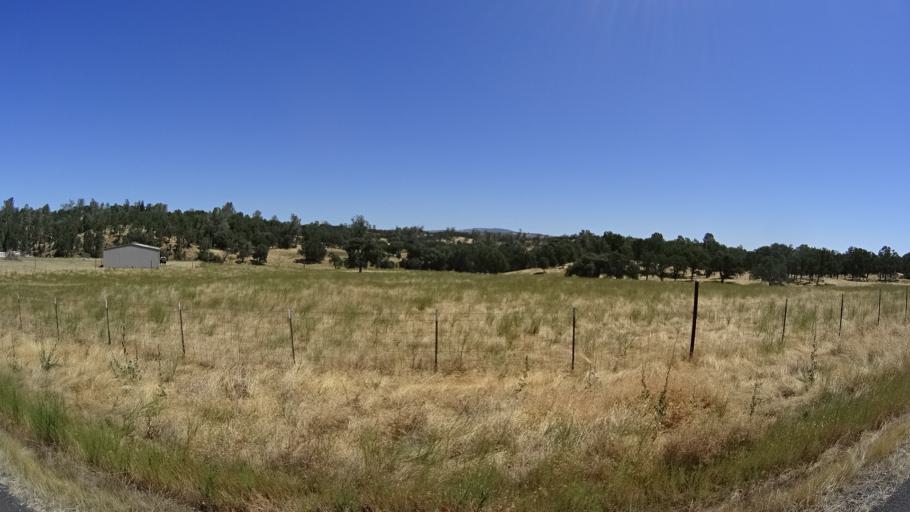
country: US
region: California
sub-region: Calaveras County
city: Copperopolis
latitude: 37.9608
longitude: -120.7000
